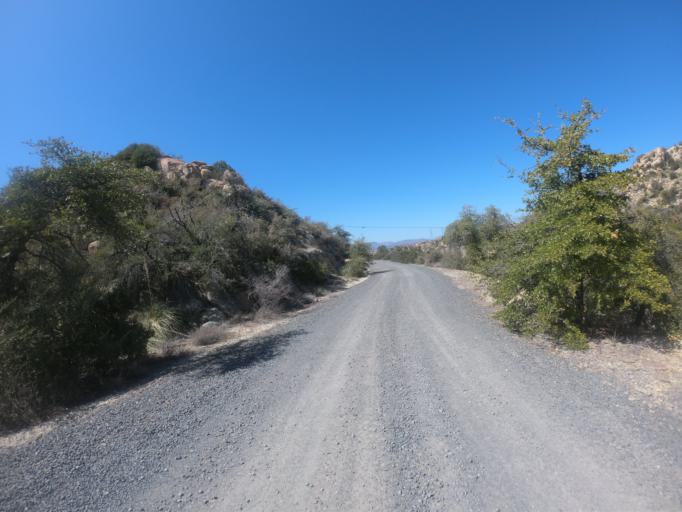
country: US
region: Arizona
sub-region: Gila County
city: Miami
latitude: 33.3555
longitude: -110.9687
